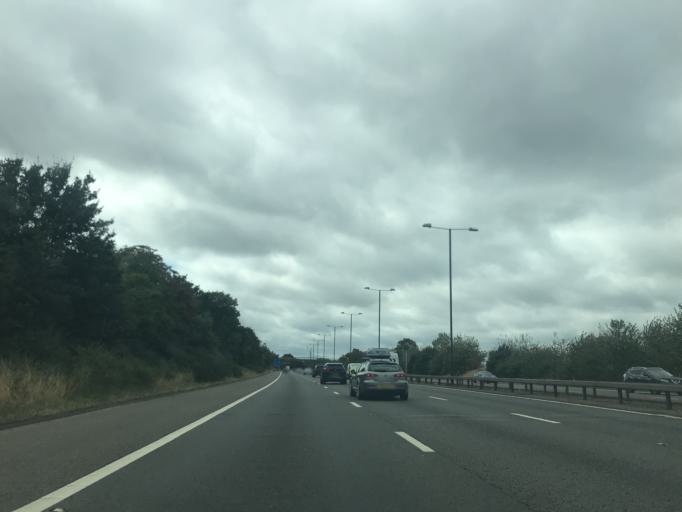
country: GB
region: England
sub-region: Greater London
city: Southall
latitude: 51.4930
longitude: -0.3585
